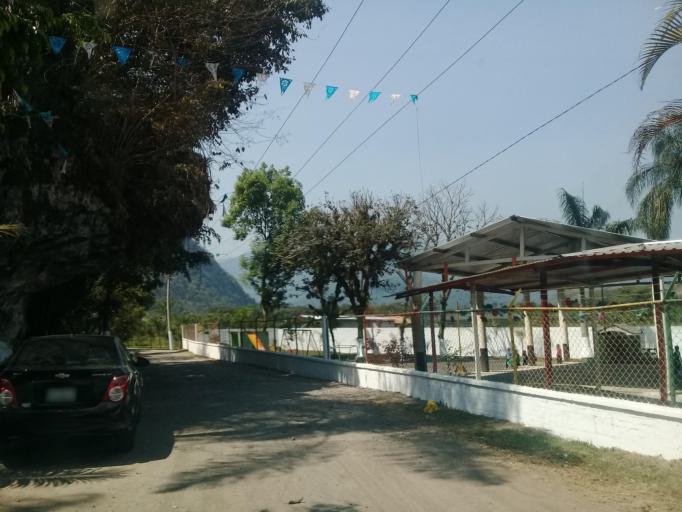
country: MX
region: Veracruz
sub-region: Ixtaczoquitlan
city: Capoluca
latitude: 18.8038
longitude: -96.9884
